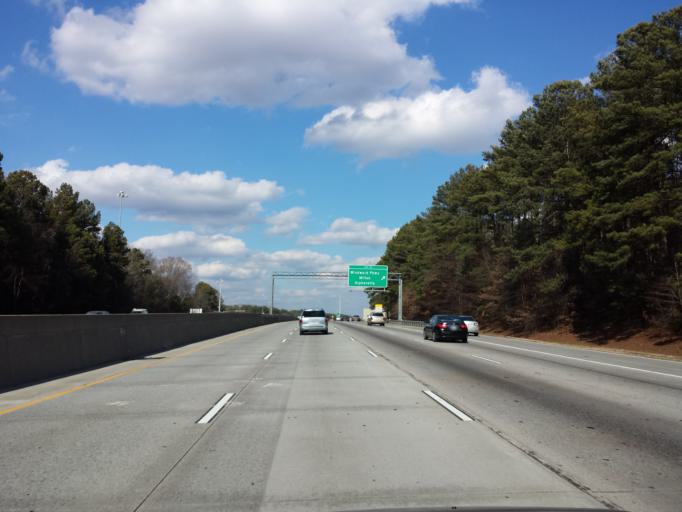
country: US
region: Georgia
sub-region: Fulton County
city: Alpharetta
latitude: 34.0820
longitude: -84.2650
